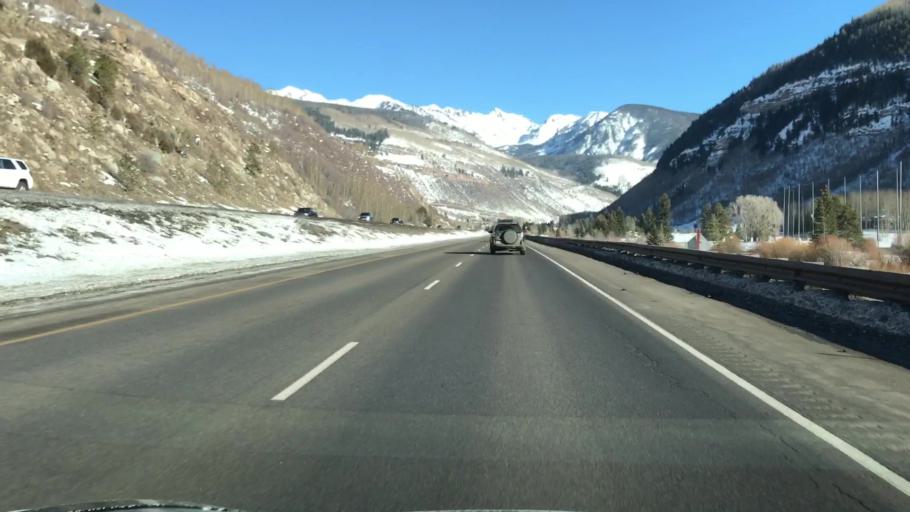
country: US
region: Colorado
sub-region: Eagle County
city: Vail
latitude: 39.6429
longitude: -106.3490
